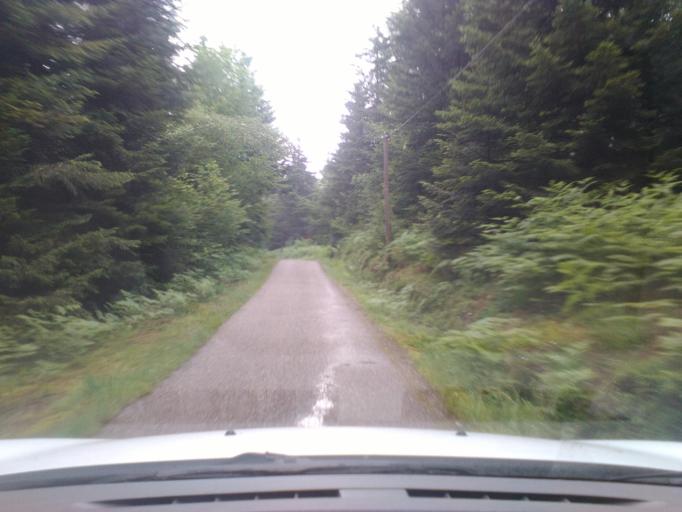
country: FR
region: Lorraine
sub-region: Departement des Vosges
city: Le Tholy
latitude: 48.1132
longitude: 6.7044
